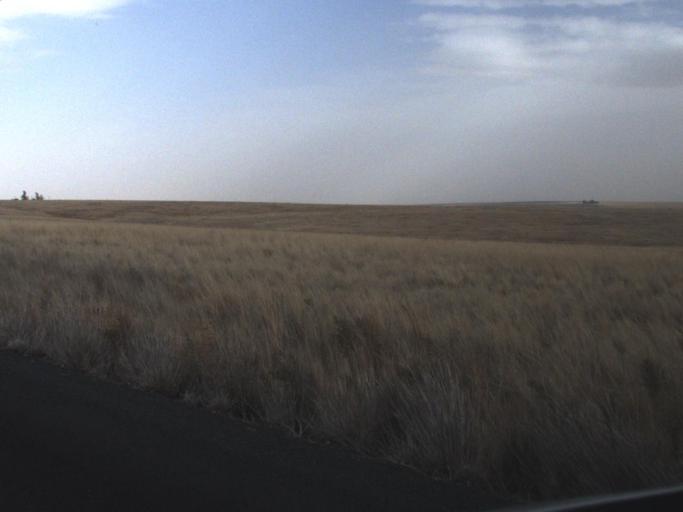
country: US
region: Washington
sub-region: Adams County
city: Ritzville
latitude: 47.3736
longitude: -118.4436
